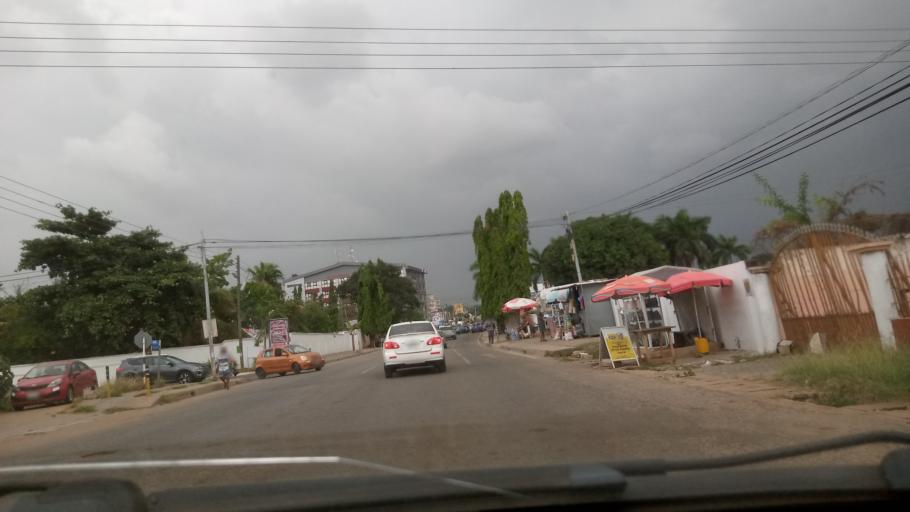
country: GH
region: Greater Accra
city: Dome
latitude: 5.6156
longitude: -0.1914
